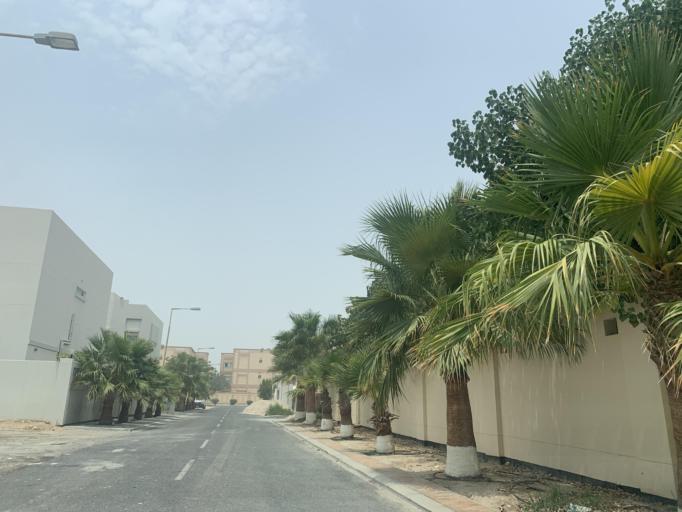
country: BH
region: Central Governorate
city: Madinat Hamad
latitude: 26.1686
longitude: 50.4687
